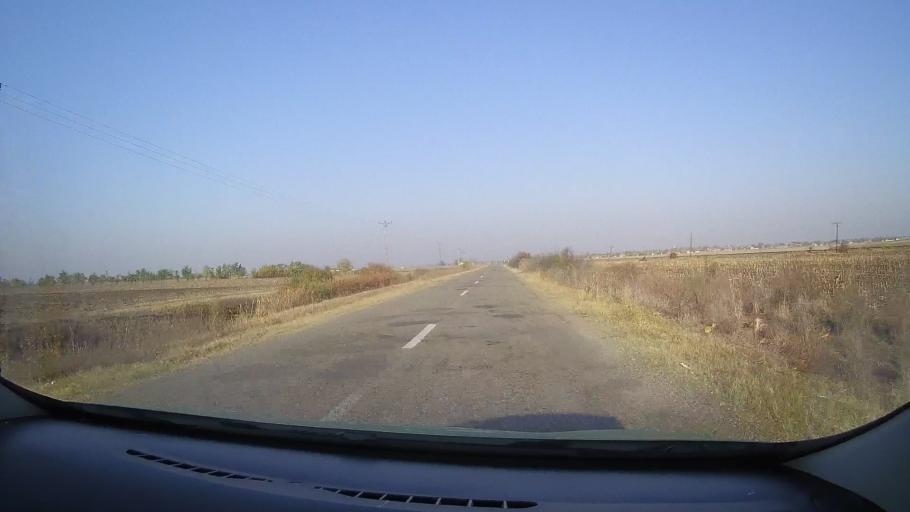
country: RO
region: Arad
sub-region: Comuna Graniceri
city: Graniceri
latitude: 46.5086
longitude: 21.3183
